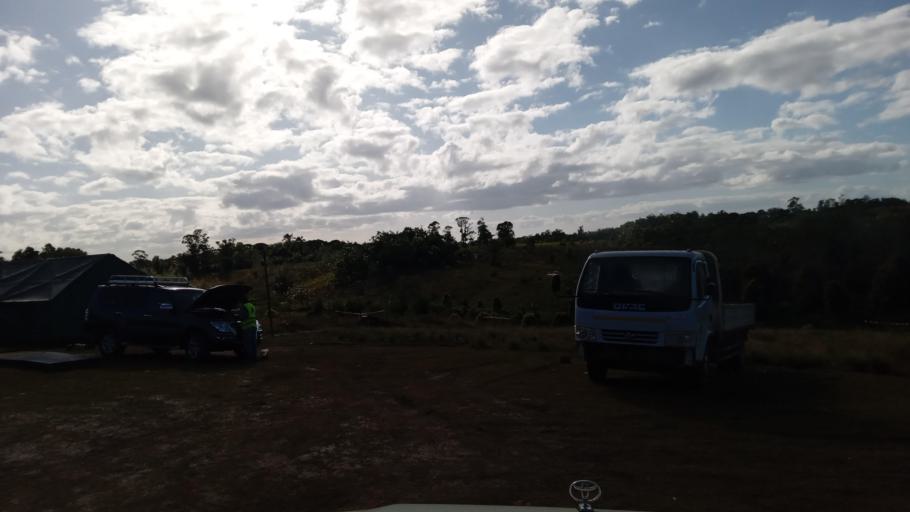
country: MG
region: Atsimo-Atsinanana
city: Vohipaho
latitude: -23.6278
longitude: 47.5835
